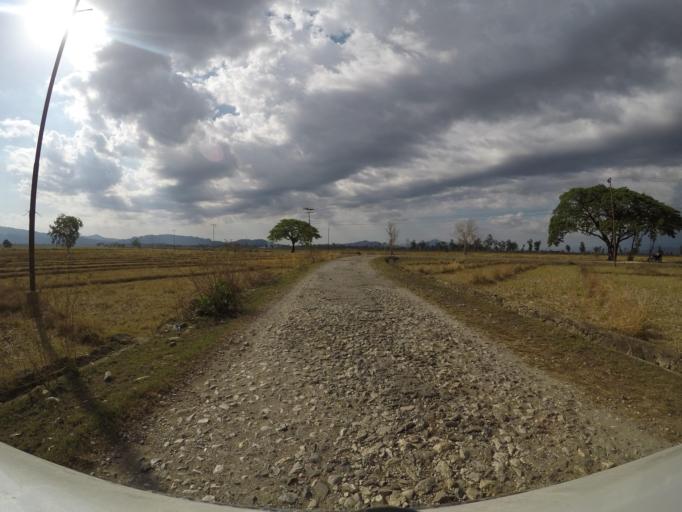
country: TL
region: Bobonaro
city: Maliana
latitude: -8.9885
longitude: 125.1665
